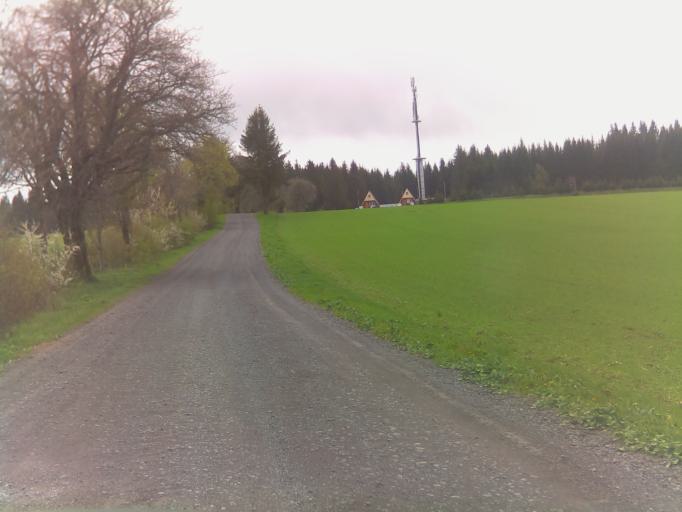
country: DE
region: Thuringia
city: Grossbreitenbach
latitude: 50.5778
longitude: 11.0175
